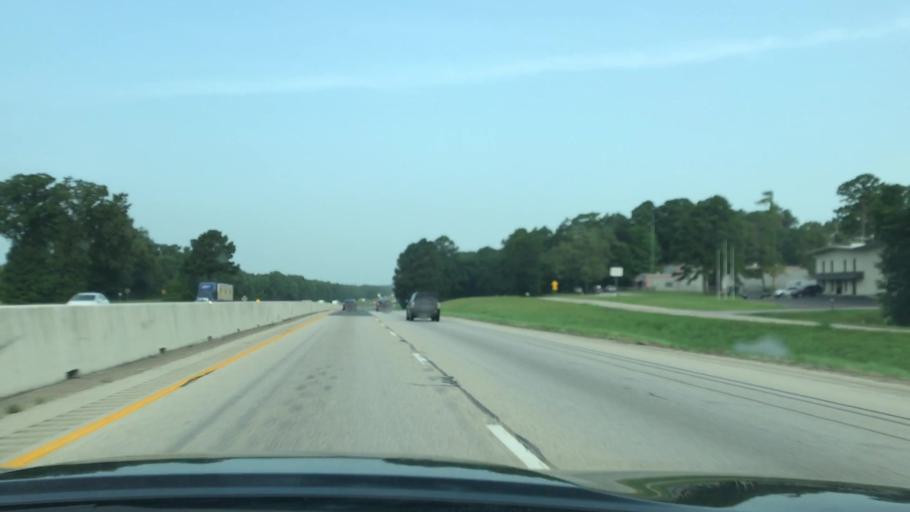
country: US
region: Texas
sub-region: Gregg County
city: Kilgore
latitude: 32.4327
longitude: -94.8665
